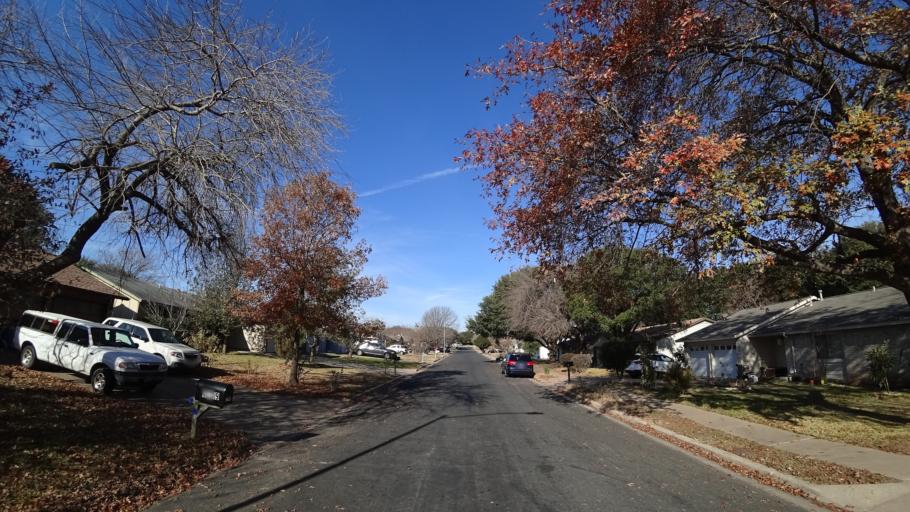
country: US
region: Texas
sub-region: Travis County
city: Wells Branch
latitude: 30.3894
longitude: -97.6997
